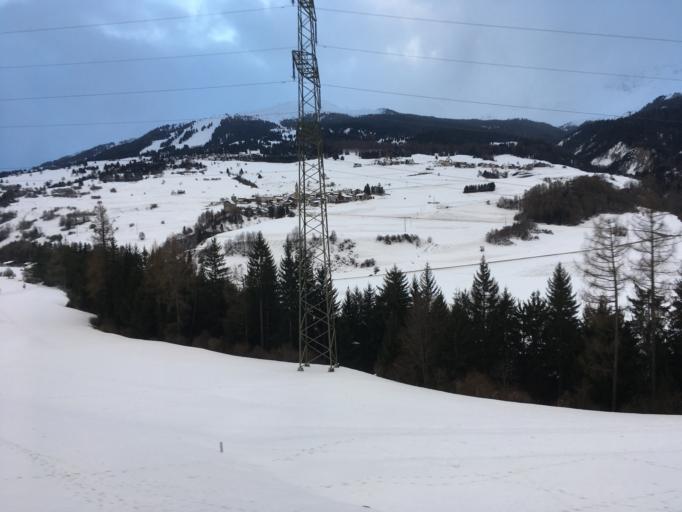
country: CH
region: Grisons
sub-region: Albula District
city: Tiefencastel
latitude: 46.6160
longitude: 9.5932
